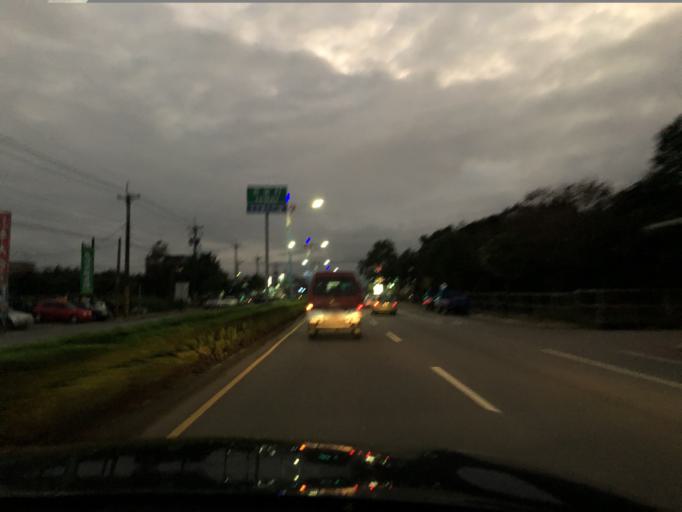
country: TW
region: Taiwan
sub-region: Hualien
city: Hualian
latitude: 23.9719
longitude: 121.5717
